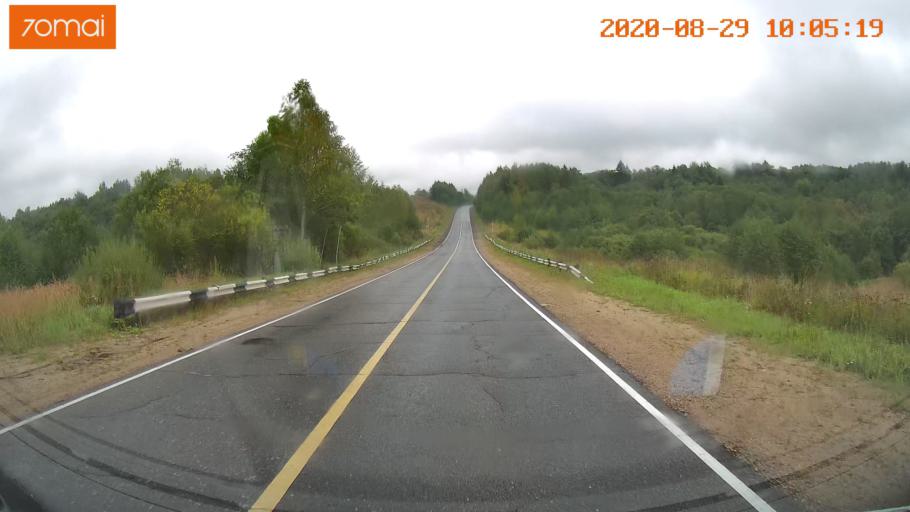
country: RU
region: Ivanovo
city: Zarechnyy
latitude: 57.3931
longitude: 42.5183
